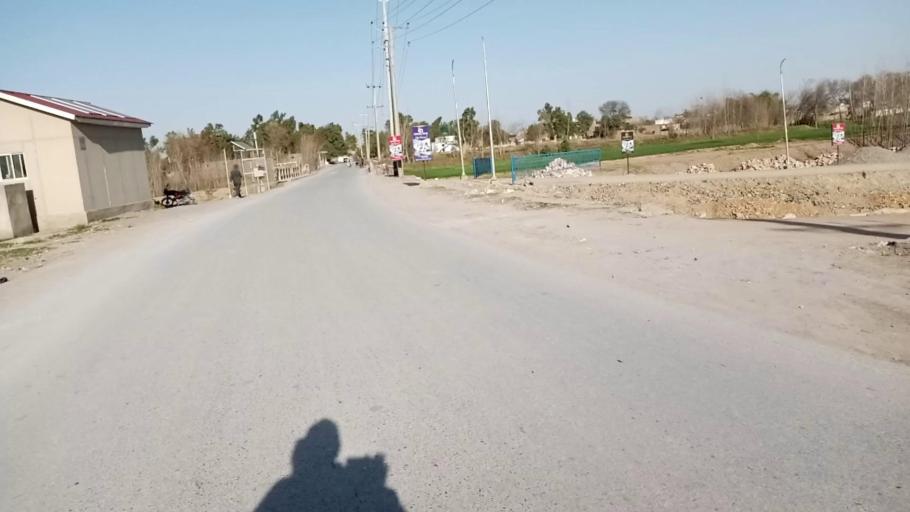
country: PK
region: Khyber Pakhtunkhwa
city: Peshawar
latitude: 34.0514
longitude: 71.5275
